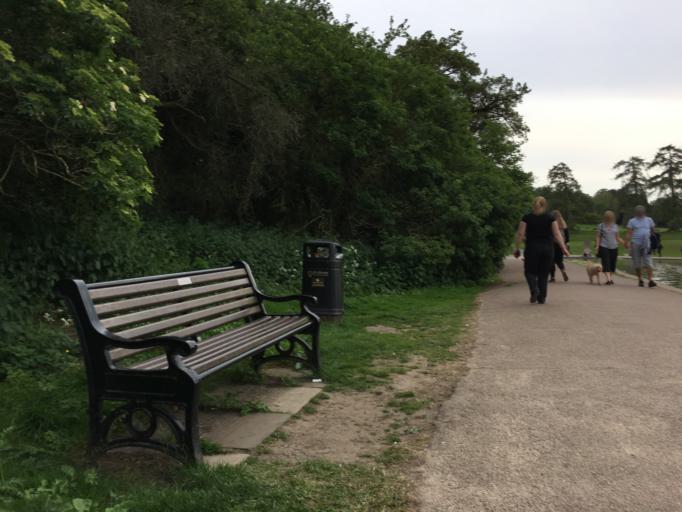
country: GB
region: England
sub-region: Hertfordshire
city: St Albans
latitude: 51.7486
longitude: -0.3488
